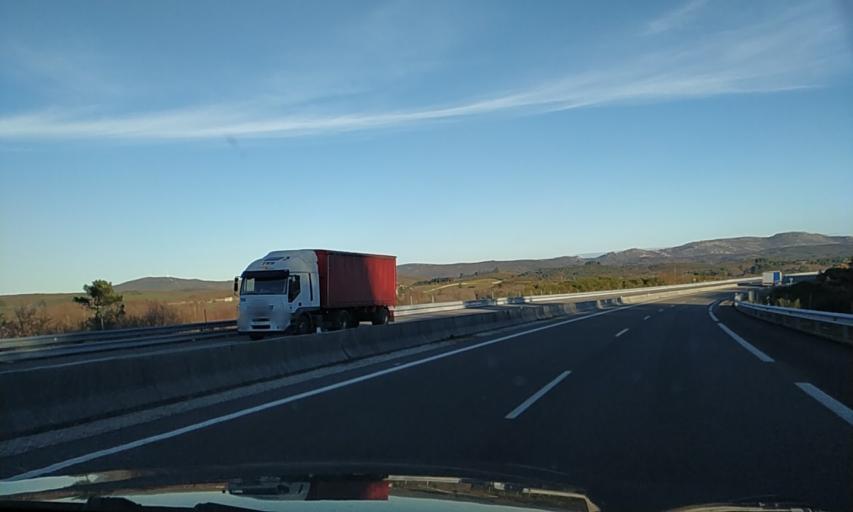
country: ES
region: Galicia
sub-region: Provincia de Pontevedra
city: Dozon
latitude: 42.5565
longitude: -8.0239
